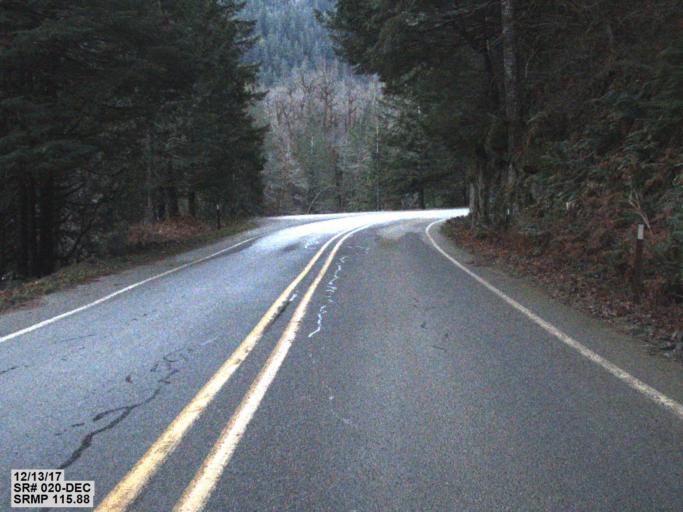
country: US
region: Washington
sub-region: Snohomish County
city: Darrington
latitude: 48.6344
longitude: -121.3217
